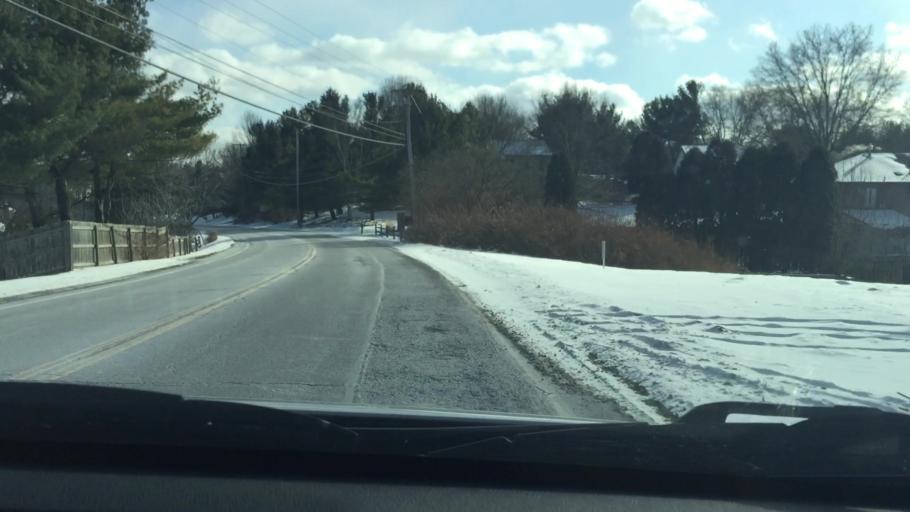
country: US
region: Pennsylvania
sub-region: Allegheny County
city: Franklin Park
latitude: 40.6043
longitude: -80.0855
